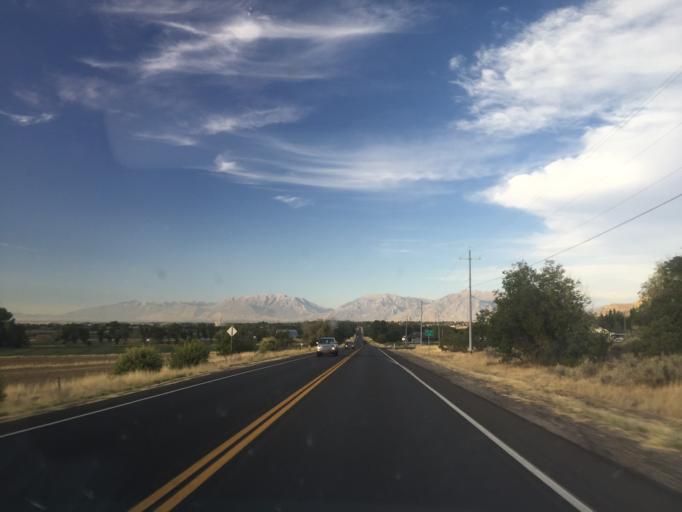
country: US
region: Utah
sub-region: Utah County
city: Santaquin
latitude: 39.9938
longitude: -111.7542
